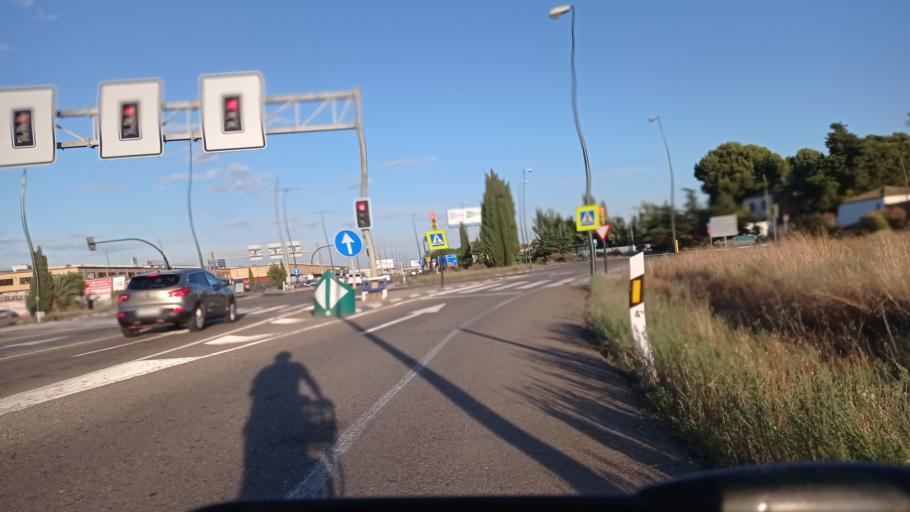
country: ES
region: Aragon
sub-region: Provincia de Zaragoza
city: Oliver-Valdefierro, Oliver, Valdefierro
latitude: 41.6733
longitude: -0.9519
